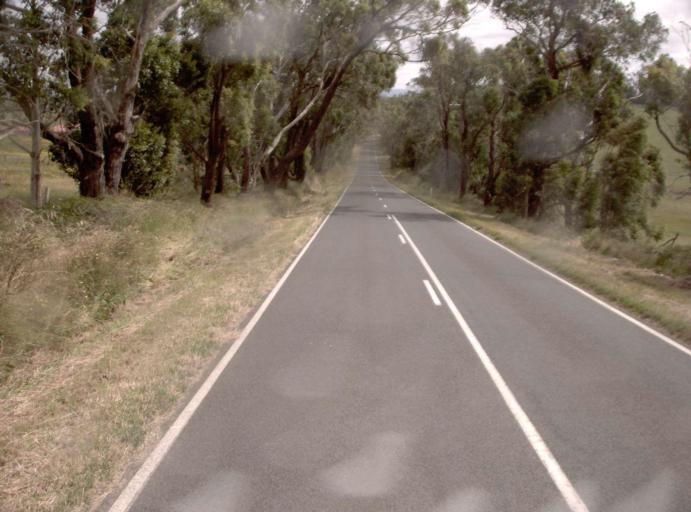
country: AU
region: Victoria
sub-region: Latrobe
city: Moe
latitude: -38.1412
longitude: 146.1471
